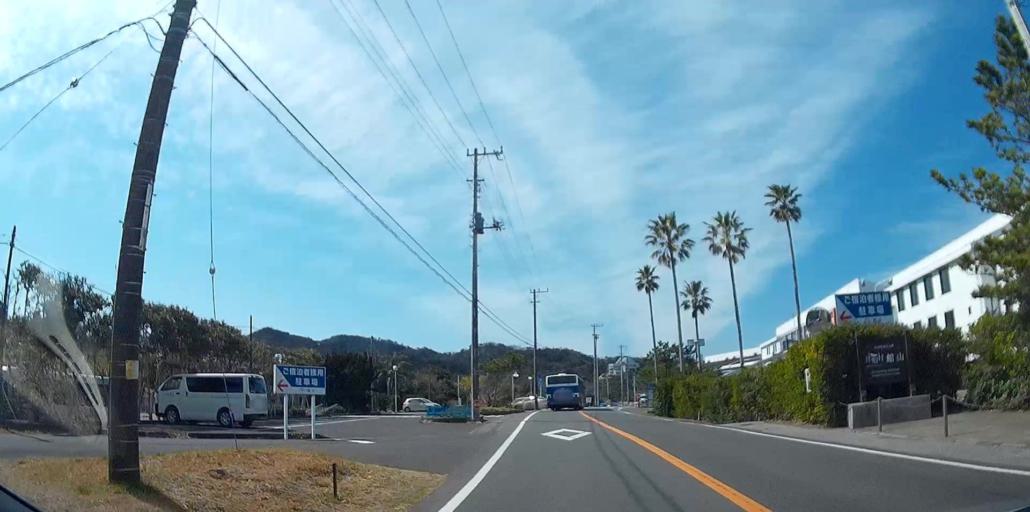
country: JP
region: Chiba
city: Tateyama
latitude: 34.9731
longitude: 139.7927
